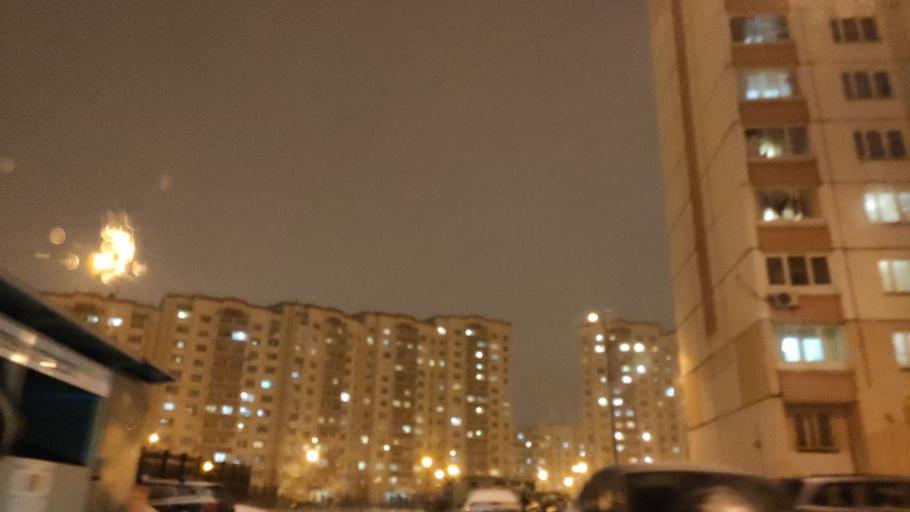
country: RU
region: Moskovskaya
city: Shcherbinka
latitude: 55.5420
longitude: 37.5645
